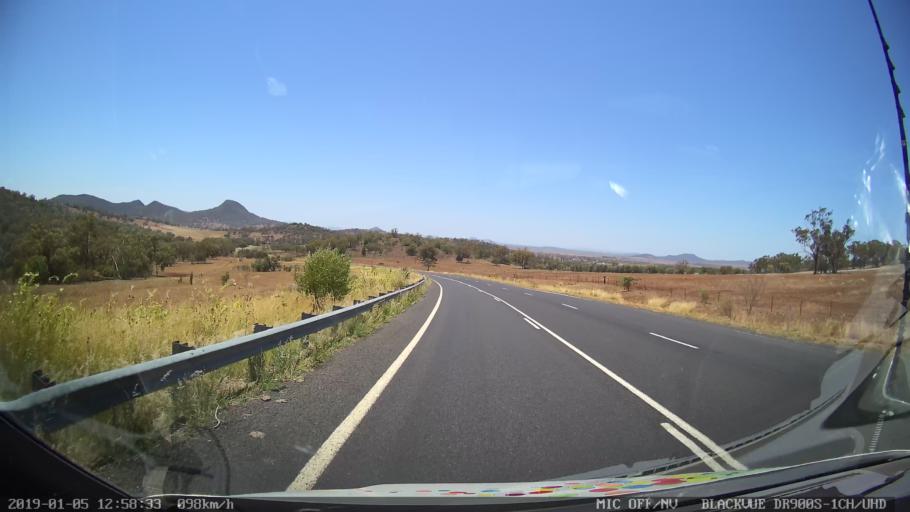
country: AU
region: New South Wales
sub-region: Narrabri
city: Boggabri
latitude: -31.1136
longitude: 149.7512
